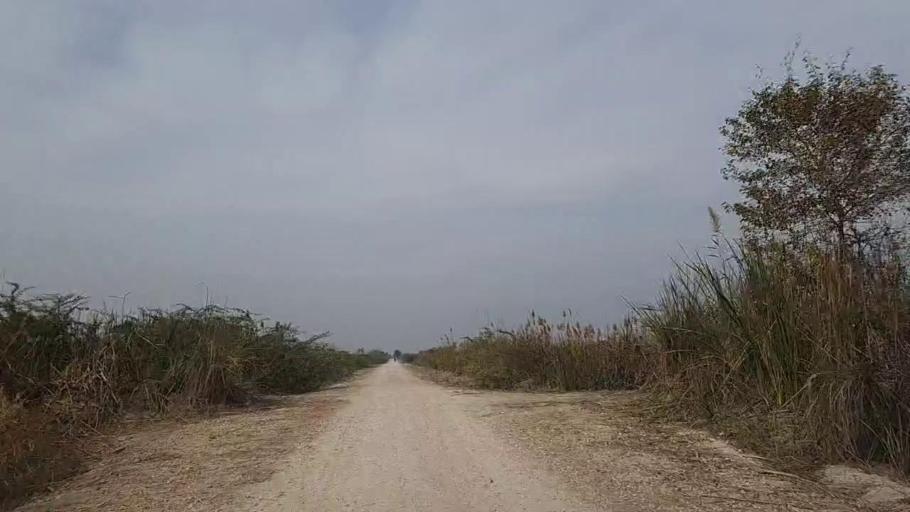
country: PK
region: Sindh
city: Daur
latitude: 26.4128
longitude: 68.4291
